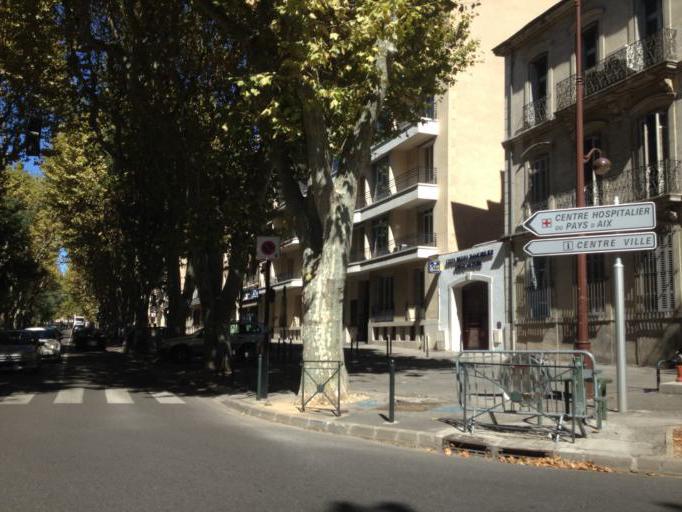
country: FR
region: Provence-Alpes-Cote d'Azur
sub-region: Departement des Bouches-du-Rhone
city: Aix-en-Provence
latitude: 43.5237
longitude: 5.4461
